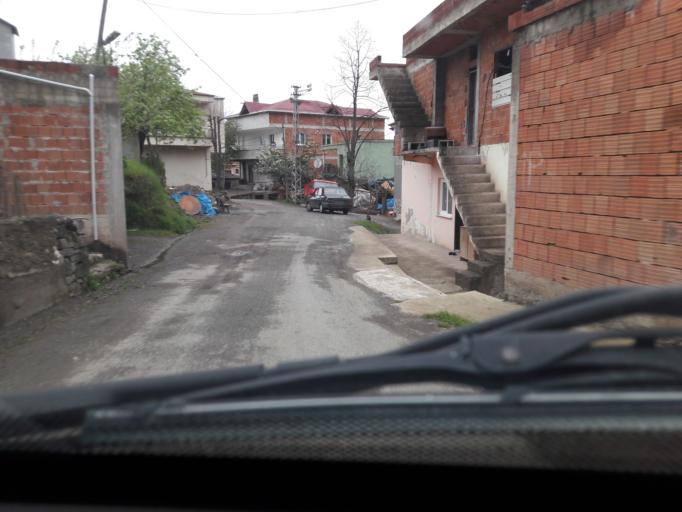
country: TR
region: Trabzon
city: Duzkoy
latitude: 40.8994
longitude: 39.4862
